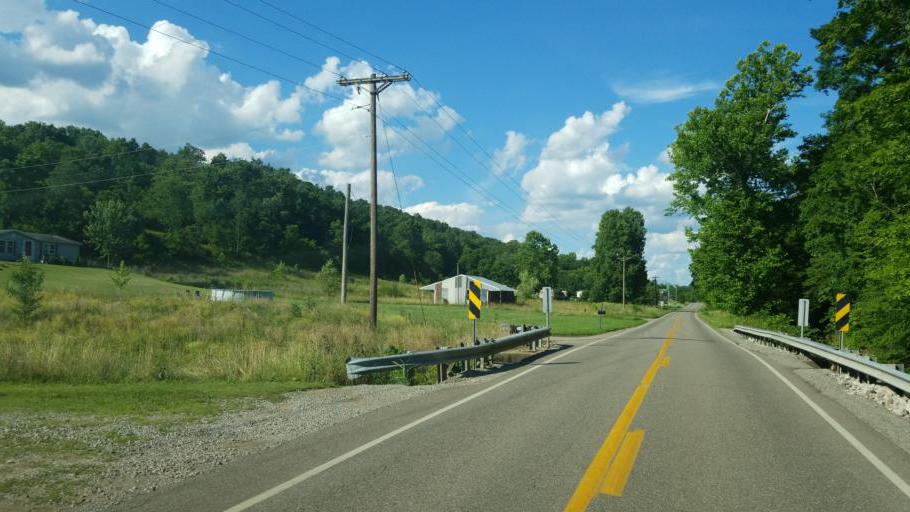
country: US
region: Ohio
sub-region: Gallia County
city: Gallipolis
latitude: 38.7782
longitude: -82.3517
